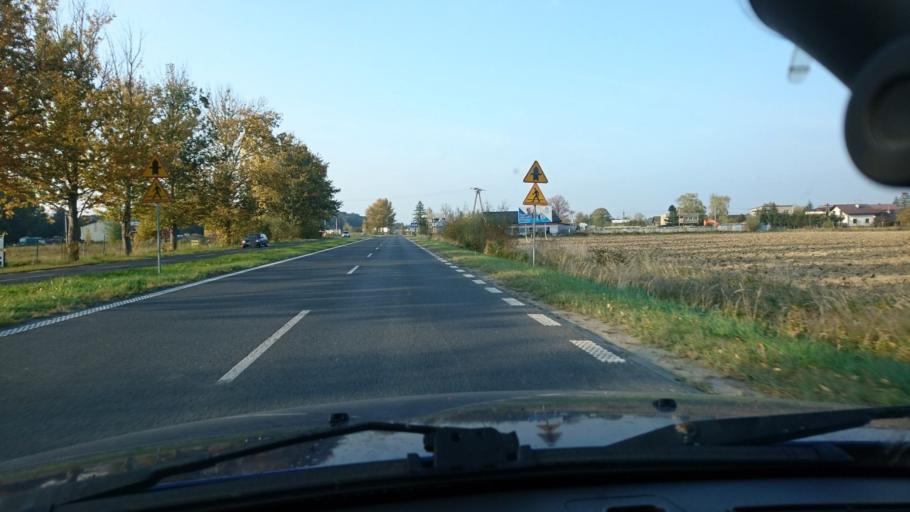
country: PL
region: Silesian Voivodeship
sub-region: Powiat cieszynski
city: Ustron
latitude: 49.7336
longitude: 18.7922
